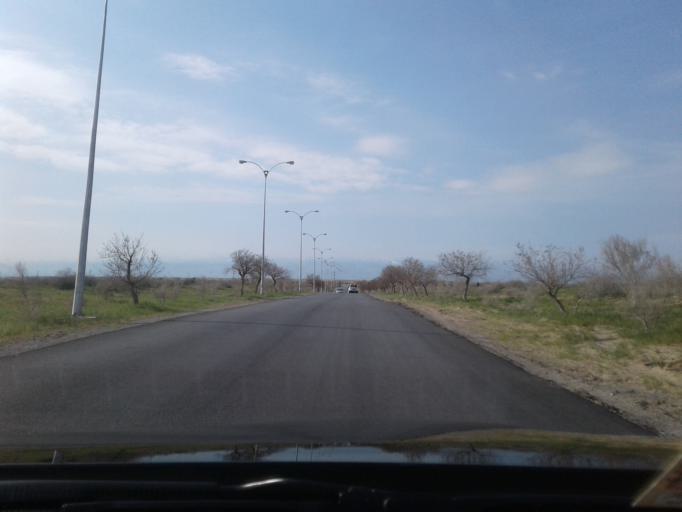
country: TM
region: Ahal
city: Ashgabat
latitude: 38.0937
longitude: 58.3838
